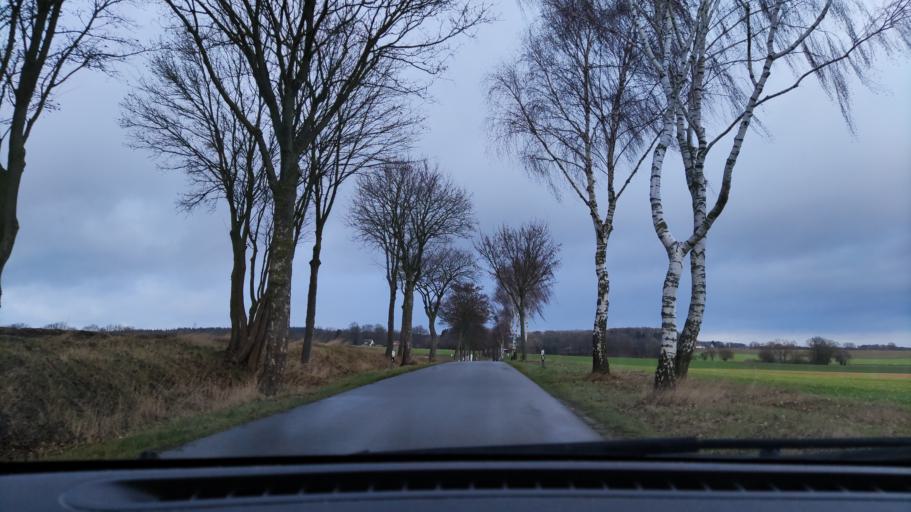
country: DE
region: Lower Saxony
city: Natendorf
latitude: 53.0876
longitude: 10.4437
